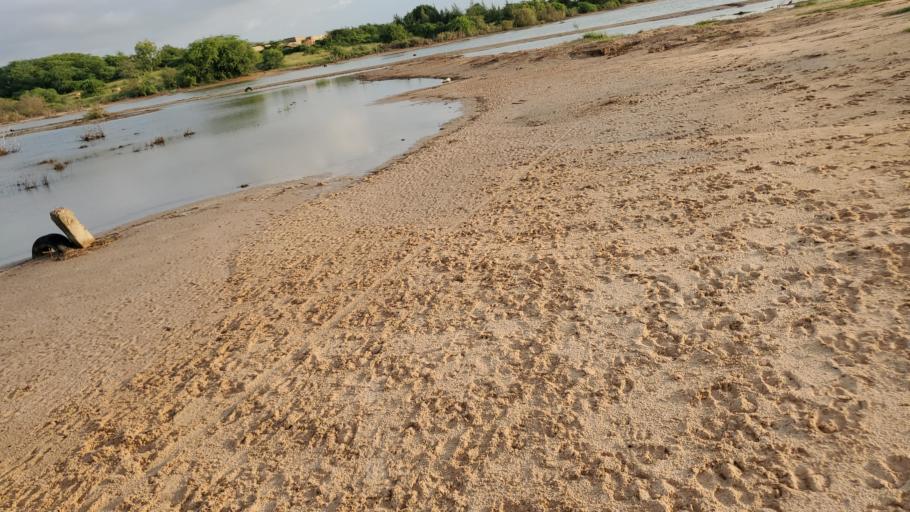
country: SN
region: Saint-Louis
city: Saint-Louis
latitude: 16.0419
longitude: -16.4181
